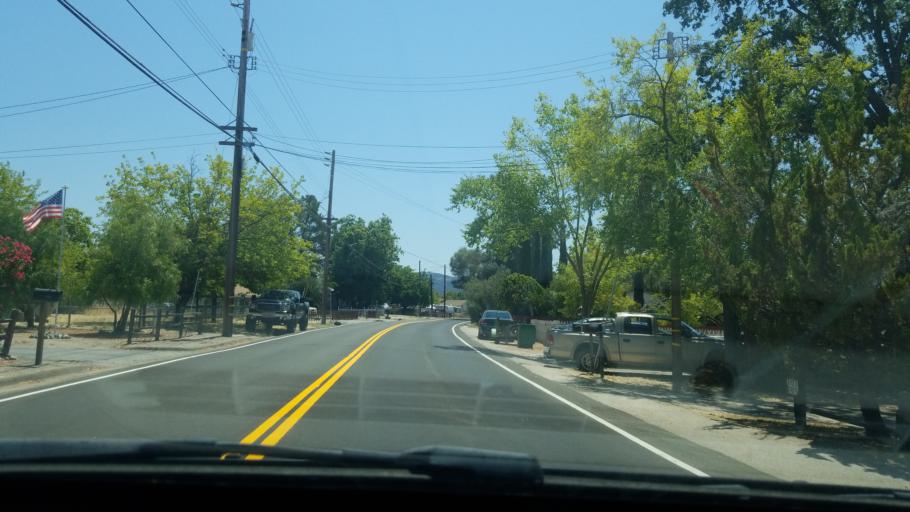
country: US
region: California
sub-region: San Luis Obispo County
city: Atascadero
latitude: 35.4804
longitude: -120.6542
